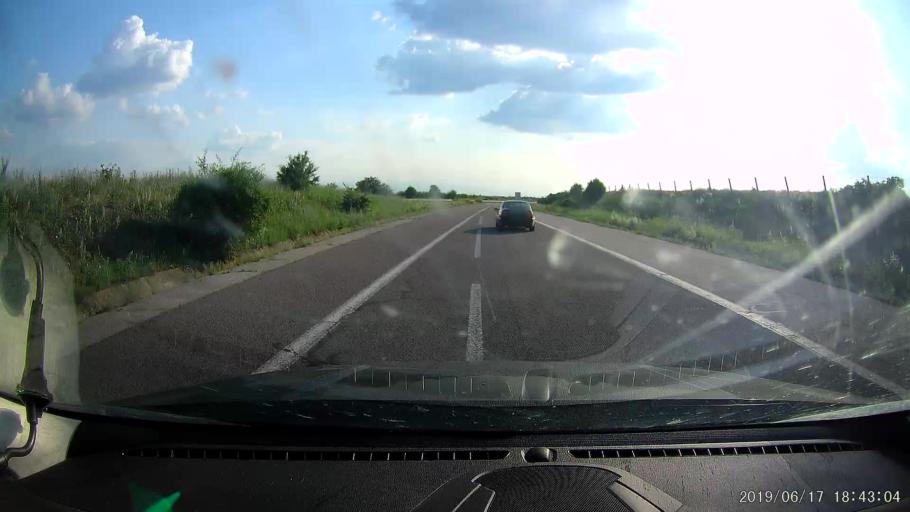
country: BG
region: Stara Zagora
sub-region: Obshtina Chirpan
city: Chirpan
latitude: 42.1934
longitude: 25.2231
